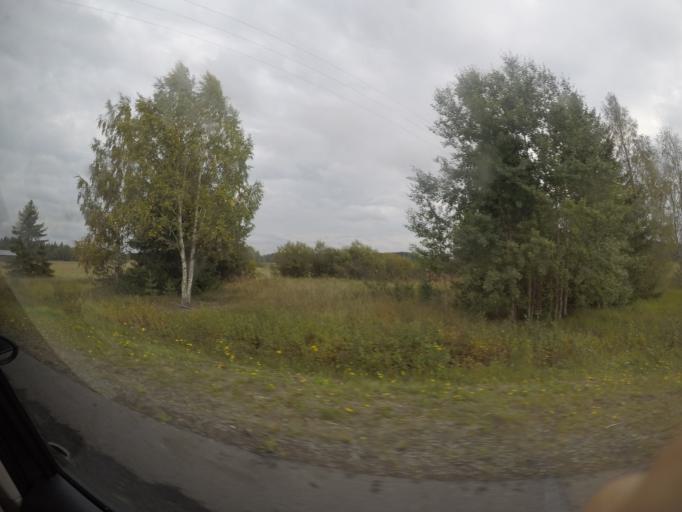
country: FI
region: Haeme
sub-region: Haemeenlinna
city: Parola
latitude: 61.0969
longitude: 24.4049
